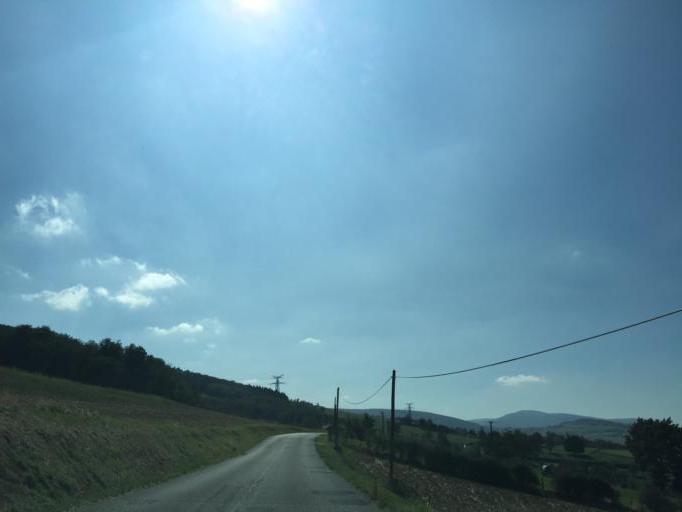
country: FR
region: Rhone-Alpes
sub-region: Departement de la Loire
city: Saint-Paul-en-Jarez
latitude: 45.4771
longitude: 4.5678
